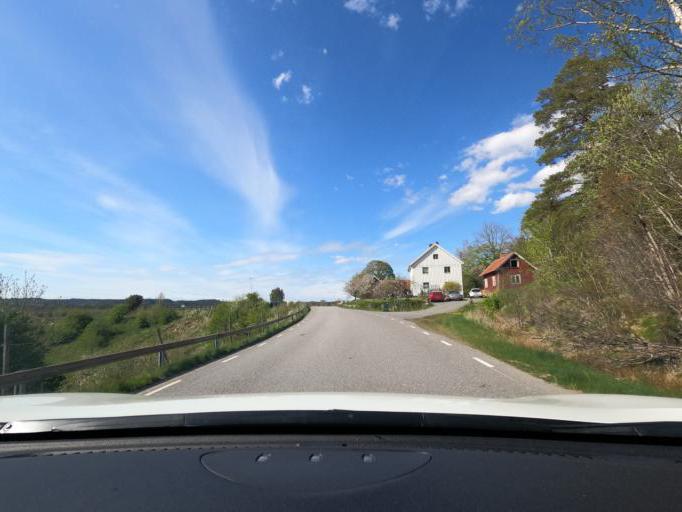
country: SE
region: Vaestra Goetaland
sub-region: Harryda Kommun
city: Ravlanda
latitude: 57.6380
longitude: 12.4968
